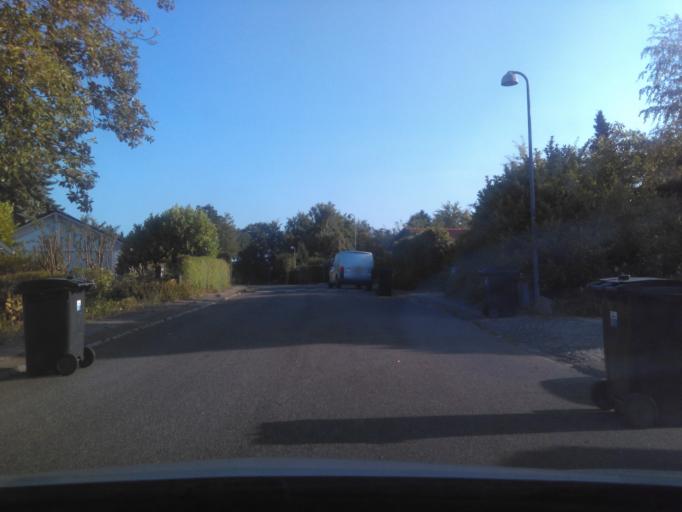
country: DK
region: Capital Region
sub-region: Fureso Kommune
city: Vaerlose
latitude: 55.7799
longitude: 12.3576
